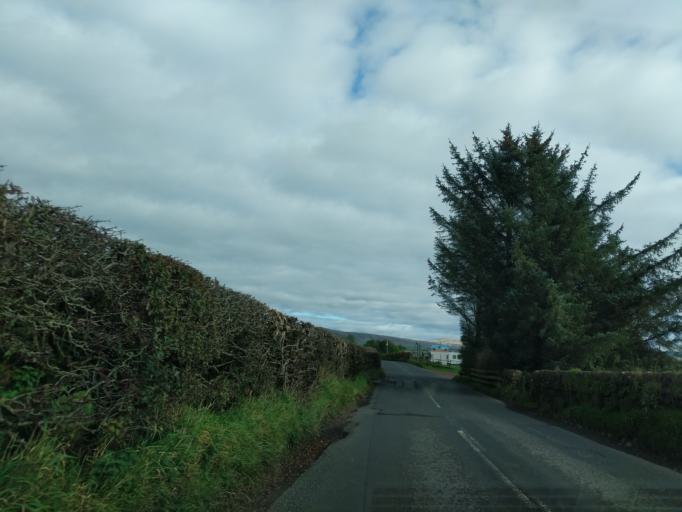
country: GB
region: Scotland
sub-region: Dumfries and Galloway
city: Thornhill
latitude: 55.2336
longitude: -3.8091
